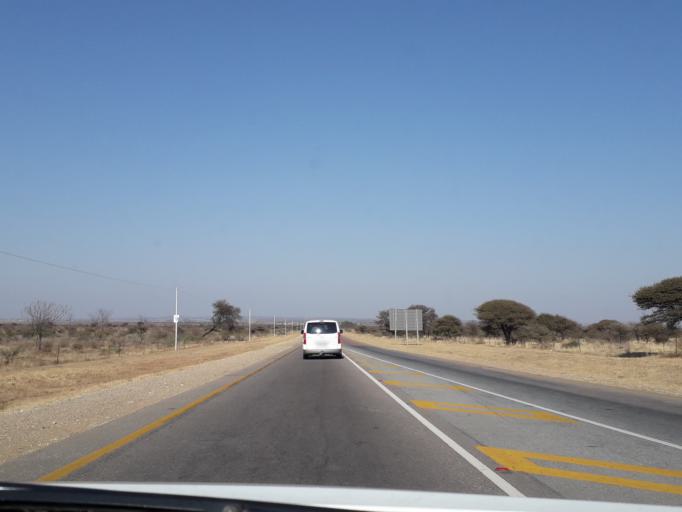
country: ZA
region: Limpopo
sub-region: Capricorn District Municipality
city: Mankoeng
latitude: -23.7586
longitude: 29.6695
